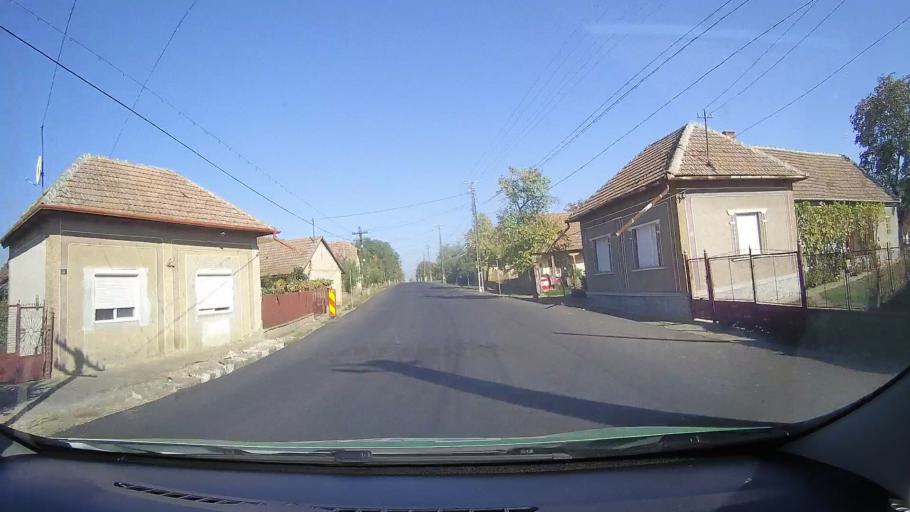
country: RO
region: Satu Mare
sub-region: Comuna Tiream
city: Tiream
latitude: 47.6185
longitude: 22.4684
